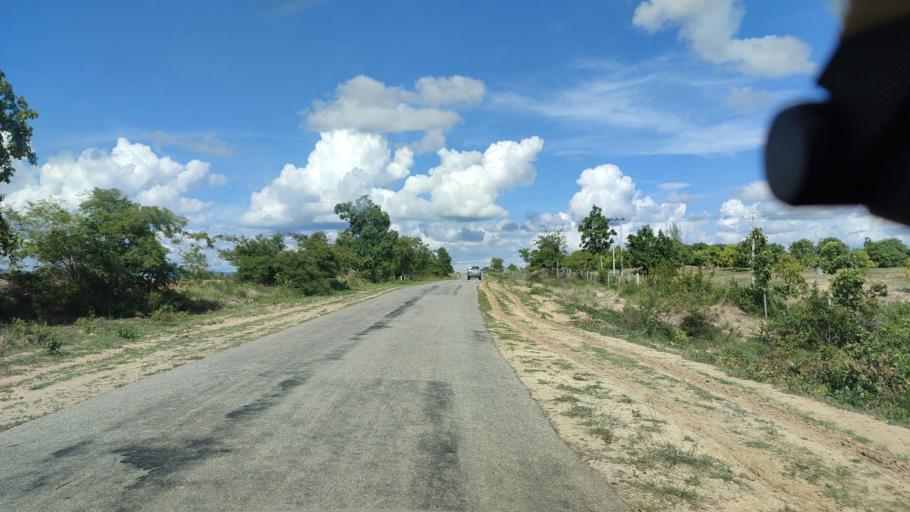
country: MM
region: Magway
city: Taungdwingyi
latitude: 20.1560
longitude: 95.5398
